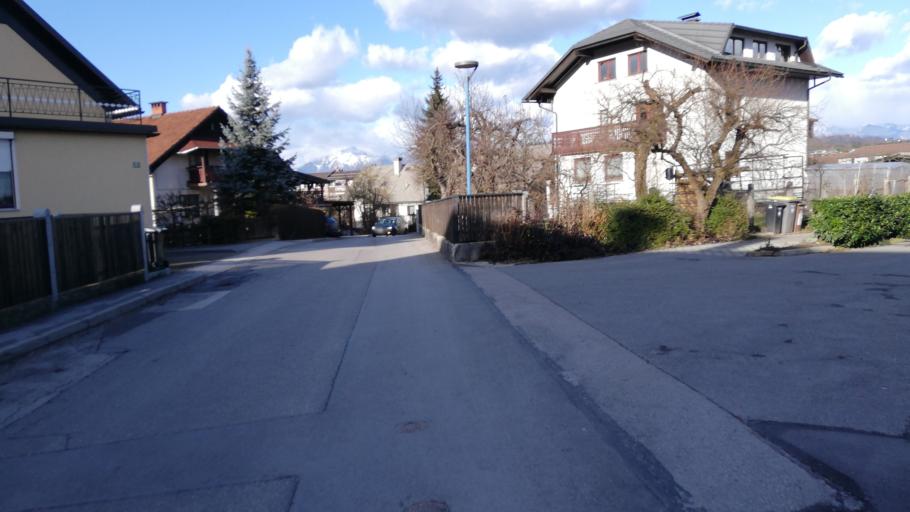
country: SI
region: Medvode
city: Medvode
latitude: 46.1323
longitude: 14.4139
